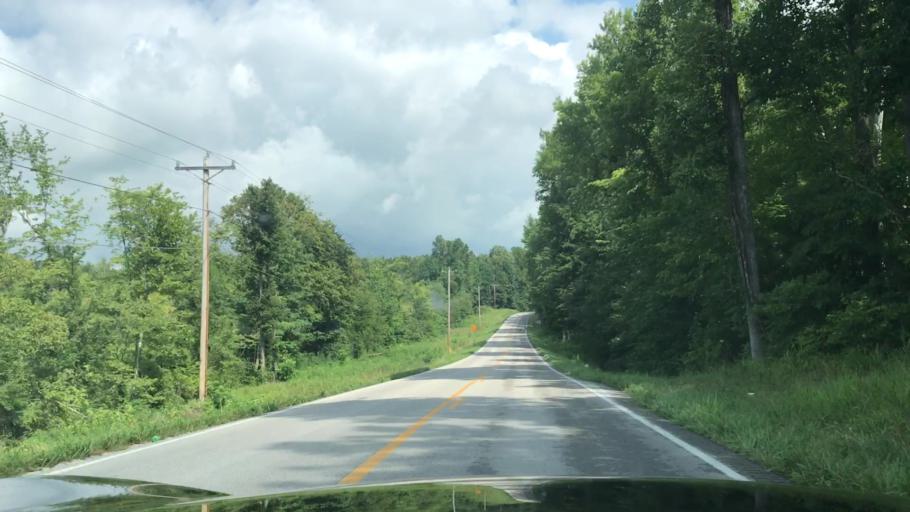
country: US
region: Kentucky
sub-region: Ohio County
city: Oak Grove
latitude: 37.1975
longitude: -86.8852
